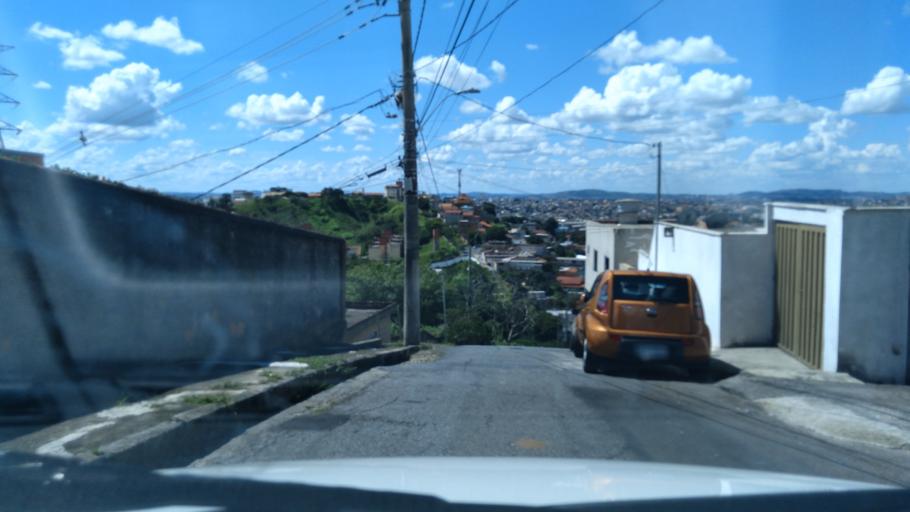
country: BR
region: Minas Gerais
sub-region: Belo Horizonte
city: Belo Horizonte
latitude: -19.8731
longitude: -43.9122
